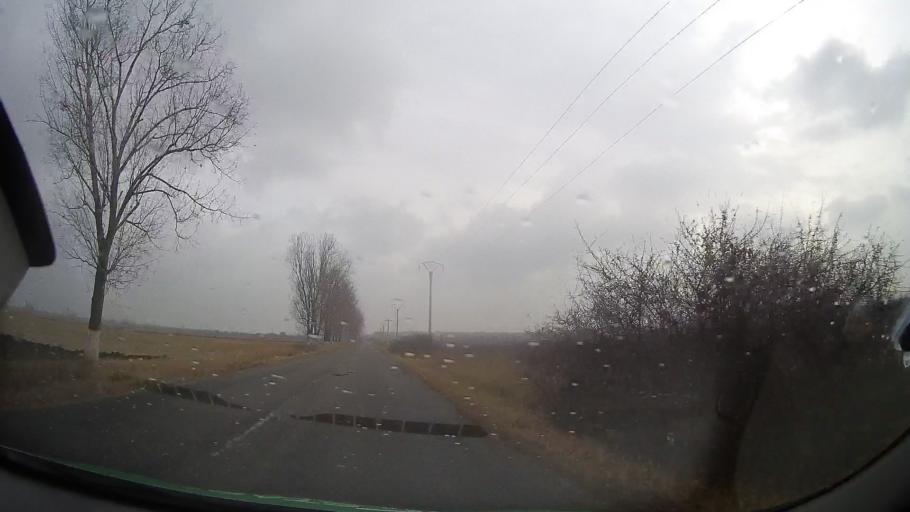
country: RO
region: Prahova
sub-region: Comuna Draganesti
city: Draganesti
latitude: 44.8336
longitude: 26.2719
